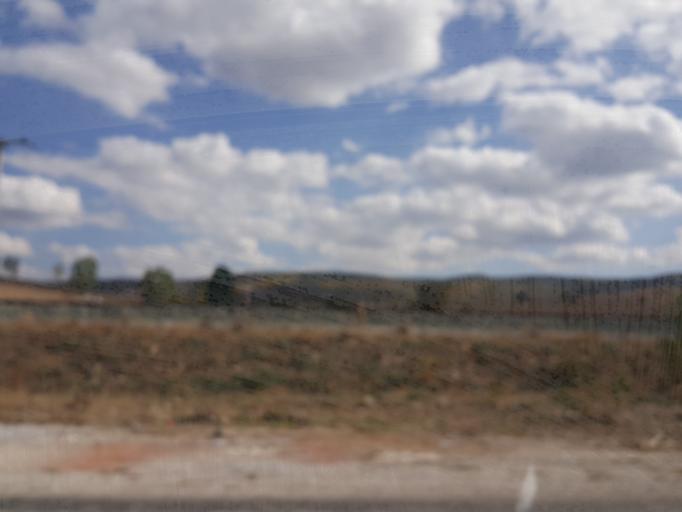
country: TR
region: Tokat
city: Yesilyurt
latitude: 40.0141
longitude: 36.2354
